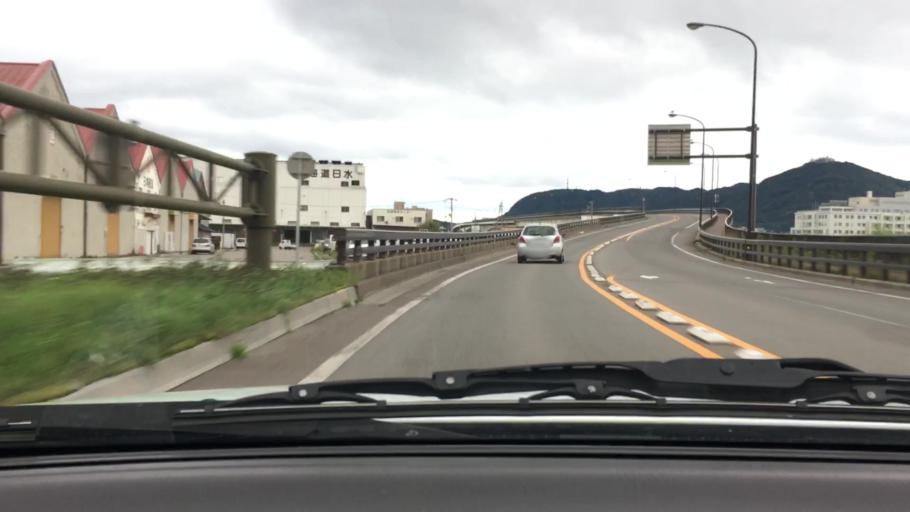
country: JP
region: Hokkaido
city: Hakodate
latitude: 41.7862
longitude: 140.7280
